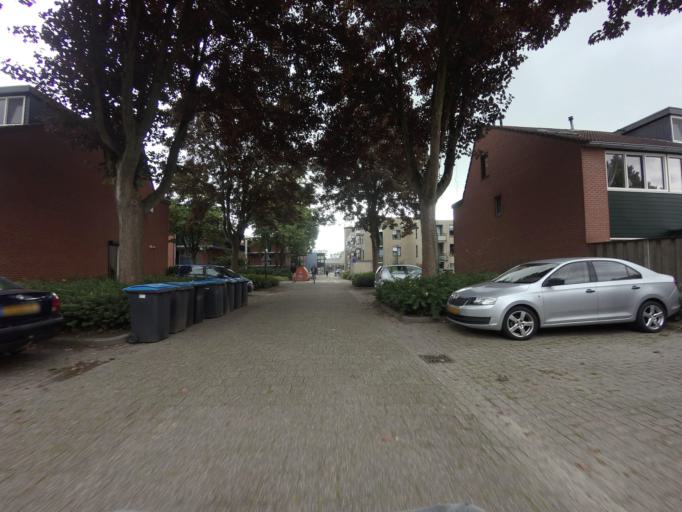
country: NL
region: Overijssel
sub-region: Gemeente Enschede
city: Enschede
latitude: 52.1950
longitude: 6.9021
